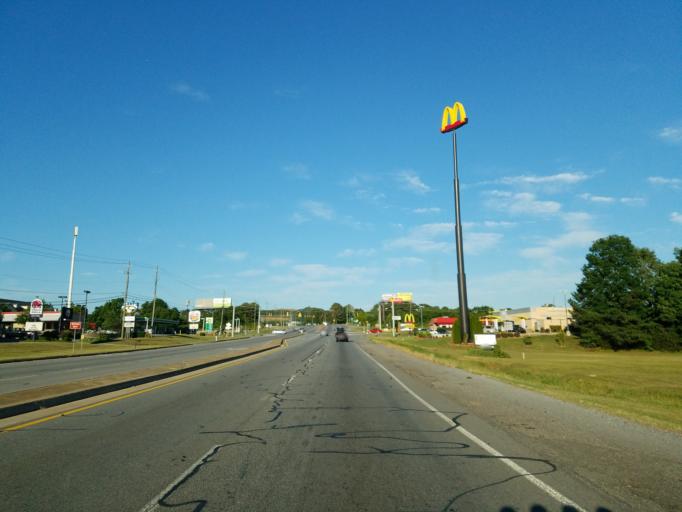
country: US
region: Georgia
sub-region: Bartow County
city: Adairsville
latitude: 34.3769
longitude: -84.9164
